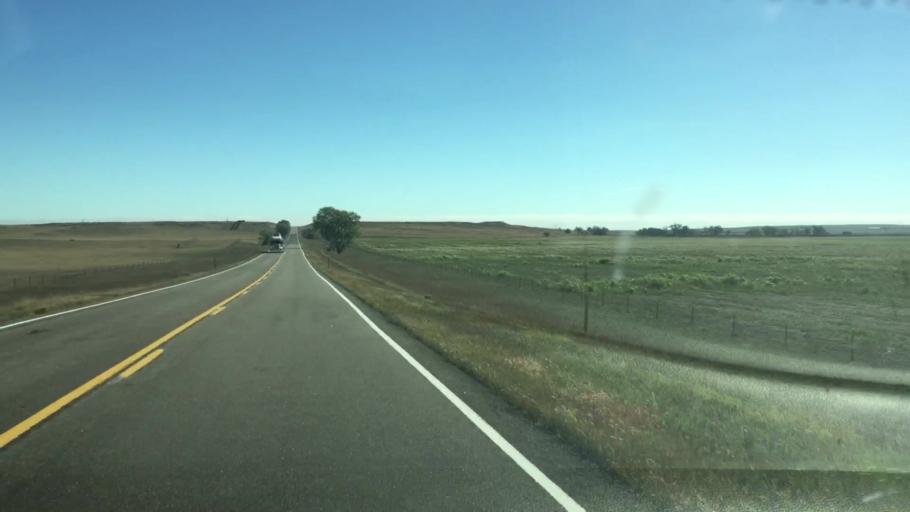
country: US
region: Colorado
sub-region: Lincoln County
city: Limon
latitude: 39.2947
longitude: -103.8947
